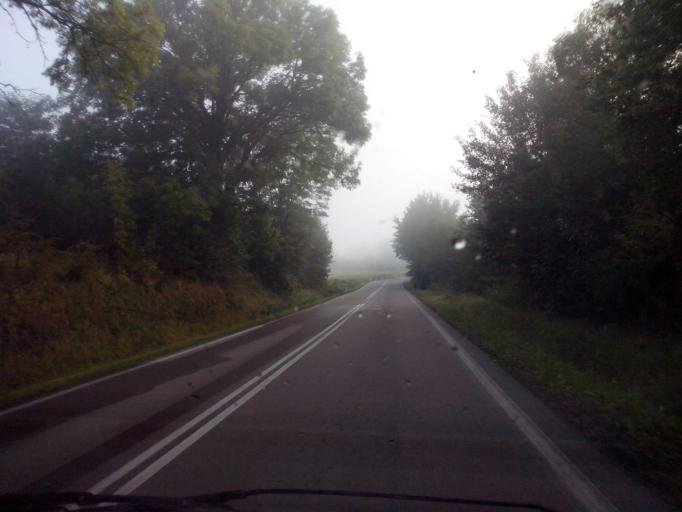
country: PL
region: Subcarpathian Voivodeship
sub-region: Powiat brzozowski
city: Domaradz
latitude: 49.8015
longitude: 21.9501
